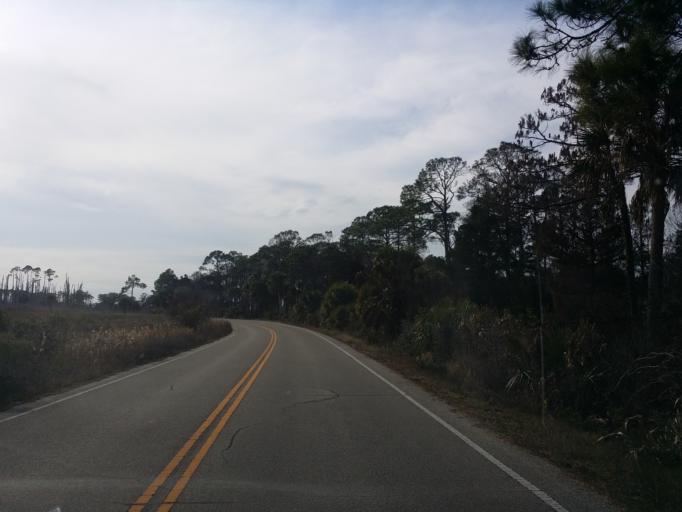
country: US
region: Florida
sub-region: Wakulla County
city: Crawfordville
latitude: 30.0969
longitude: -84.1614
